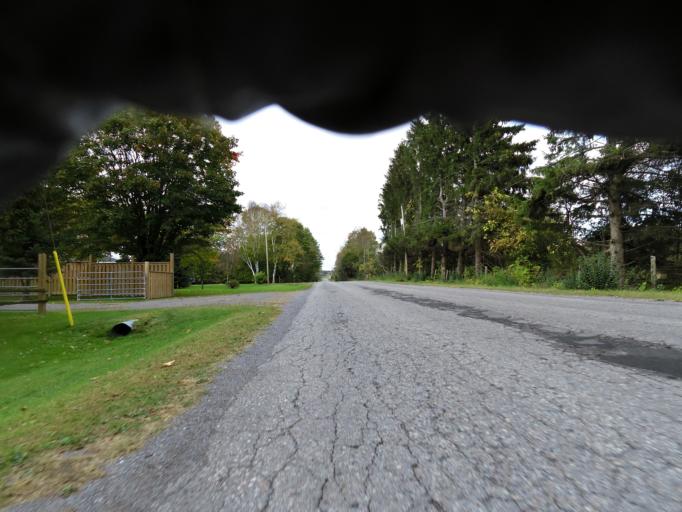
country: CA
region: Ontario
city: Cobourg
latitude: 43.9800
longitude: -77.9692
